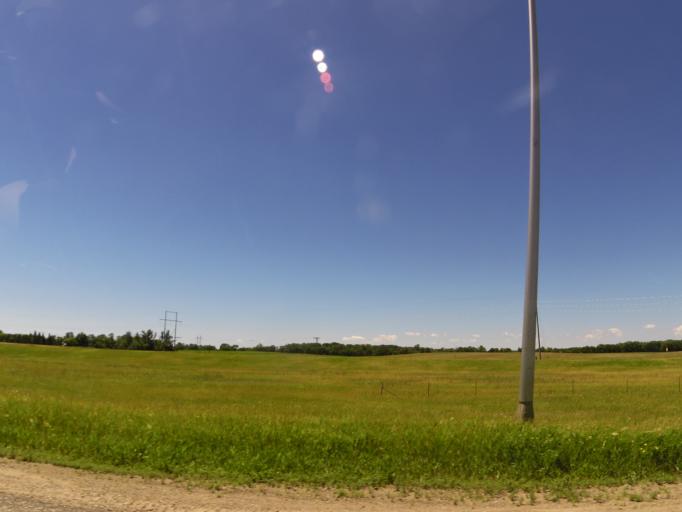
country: US
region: Minnesota
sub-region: Becker County
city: Frazee
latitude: 46.7213
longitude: -95.7195
